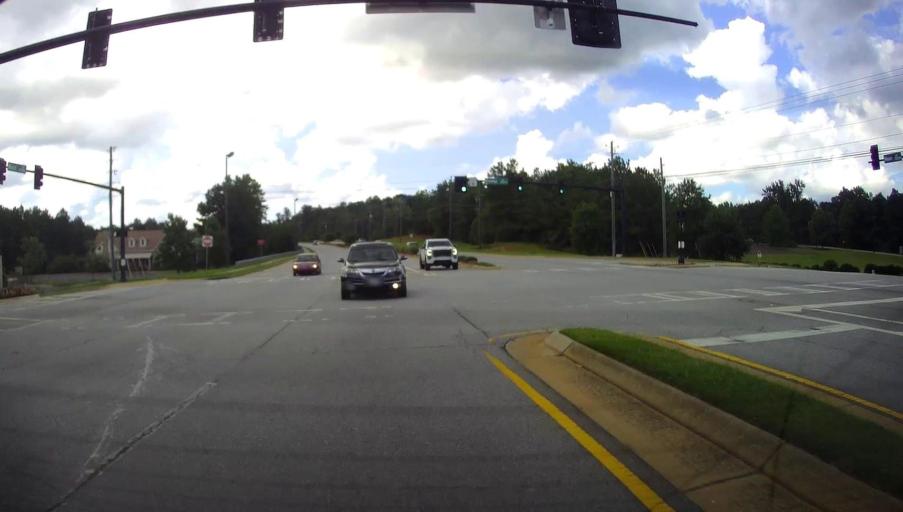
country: US
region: Alabama
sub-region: Russell County
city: Phenix City
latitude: 32.5560
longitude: -84.9274
